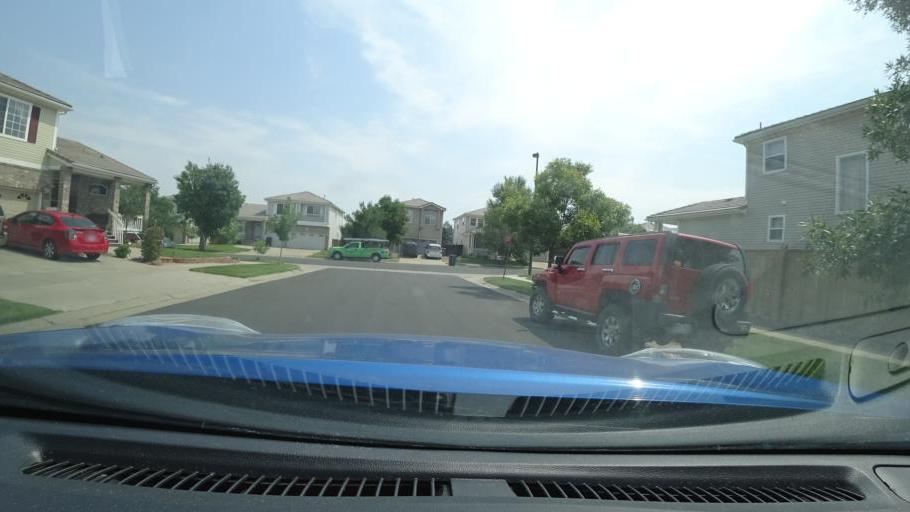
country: US
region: Colorado
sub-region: Adams County
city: Aurora
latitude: 39.7822
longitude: -104.7508
